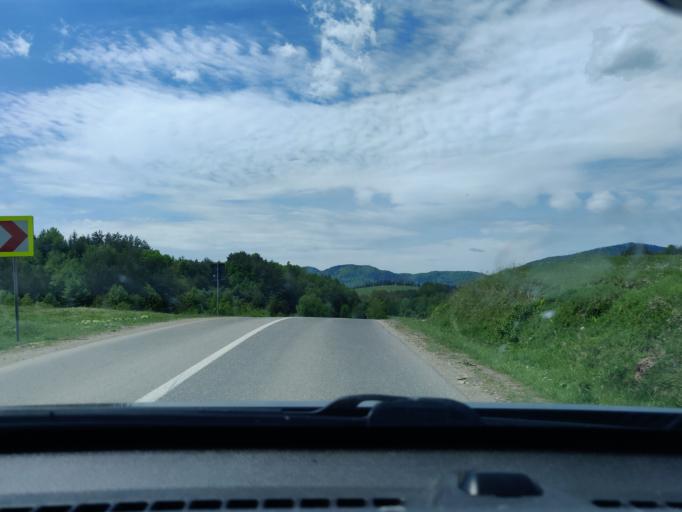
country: RO
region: Vrancea
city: Dragosloveni
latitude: 46.0058
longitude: 26.6793
